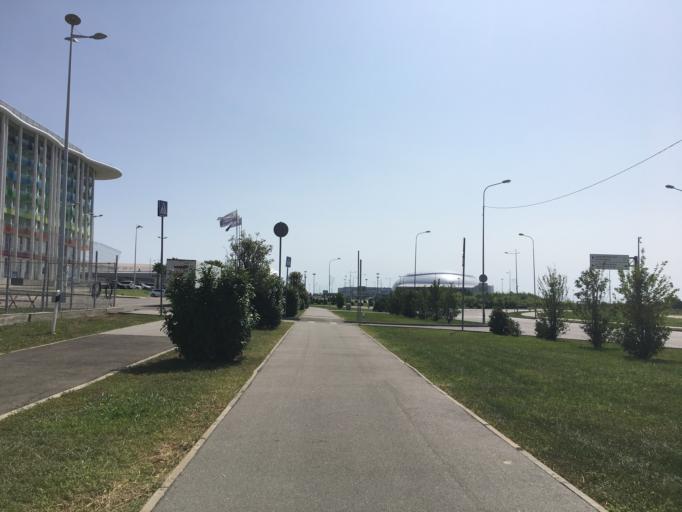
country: RU
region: Krasnodarskiy
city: Adler
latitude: 43.4127
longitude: 39.9489
